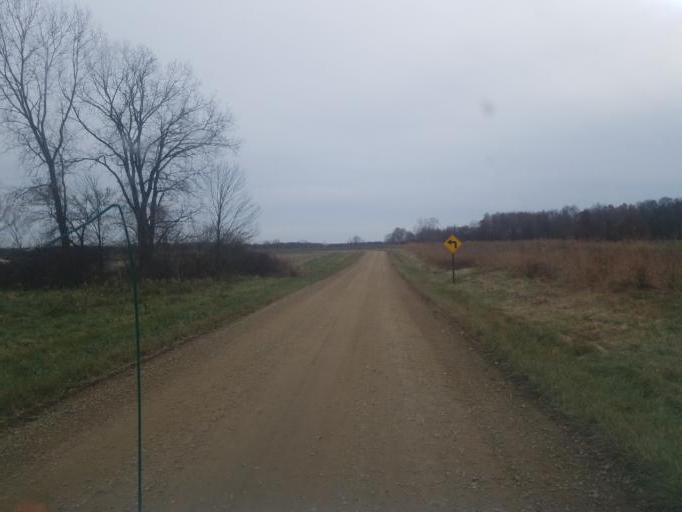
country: US
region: Ohio
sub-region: Knox County
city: Fredericktown
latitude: 40.4109
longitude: -82.6354
